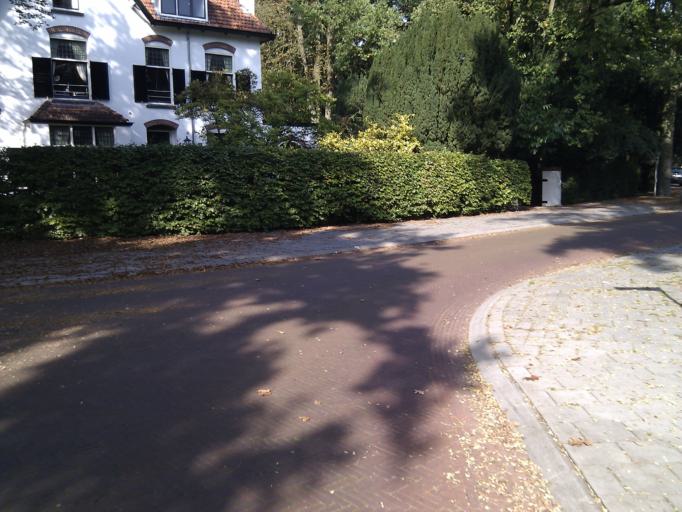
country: NL
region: Utrecht
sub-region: Gemeente De Bilt
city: De Bilt
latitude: 52.1272
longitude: 5.2007
